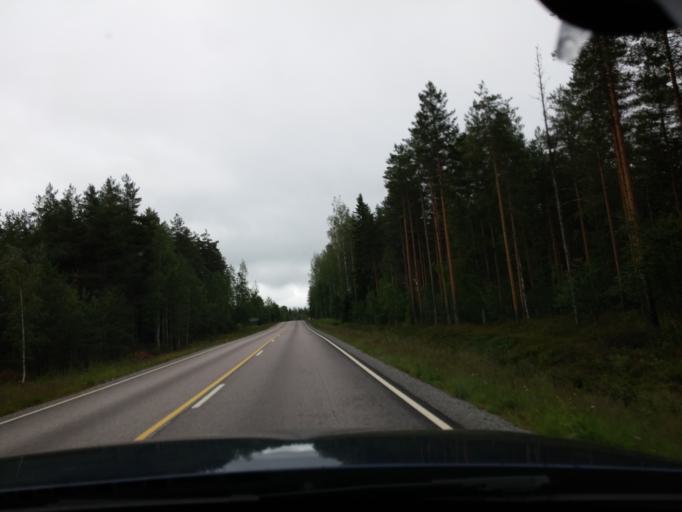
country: FI
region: Central Finland
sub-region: Saarijaervi-Viitasaari
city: Pylkoenmaeki
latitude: 62.6224
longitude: 24.7780
